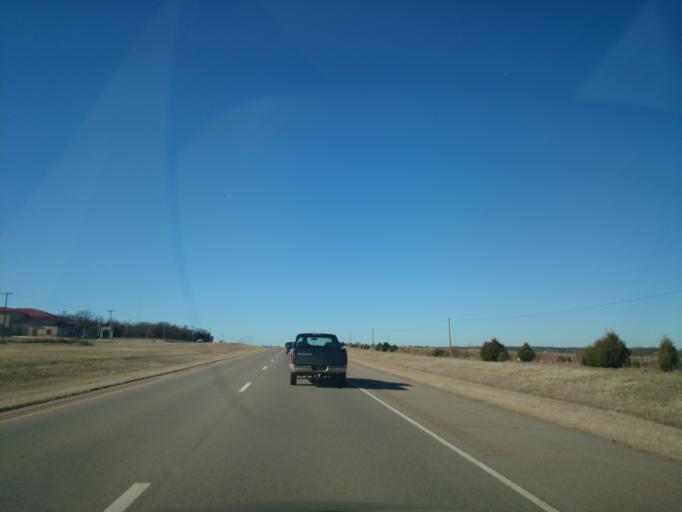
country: US
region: Oklahoma
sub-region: Payne County
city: Stillwater
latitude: 36.1162
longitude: -97.1600
